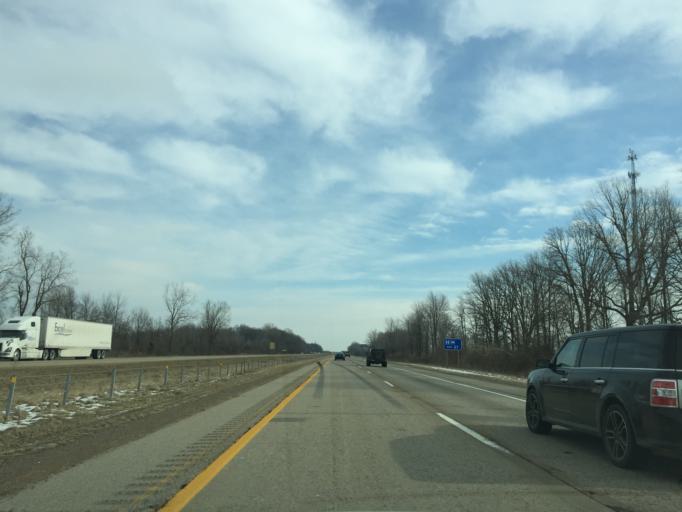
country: US
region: Michigan
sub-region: Ionia County
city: Lake Odessa
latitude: 42.8792
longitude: -85.0993
